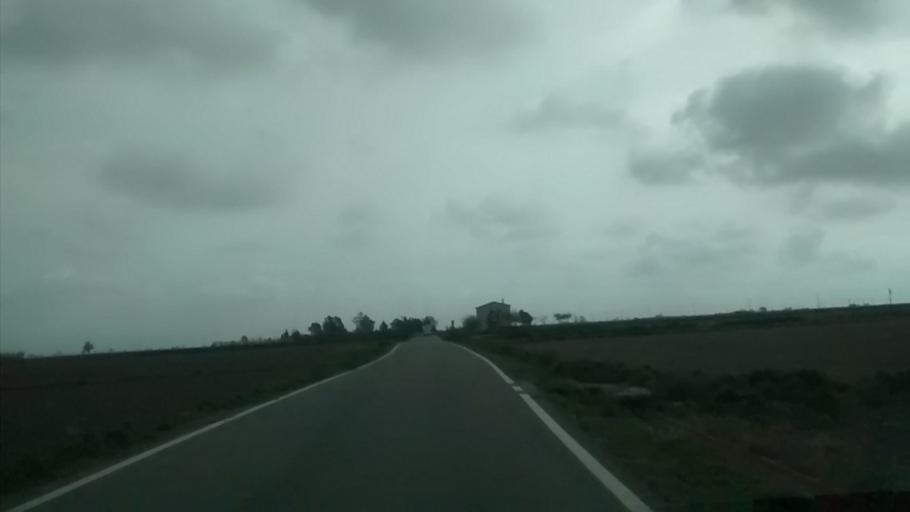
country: ES
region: Catalonia
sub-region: Provincia de Tarragona
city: Sant Carles de la Rapita
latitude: 40.6506
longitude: 0.6200
